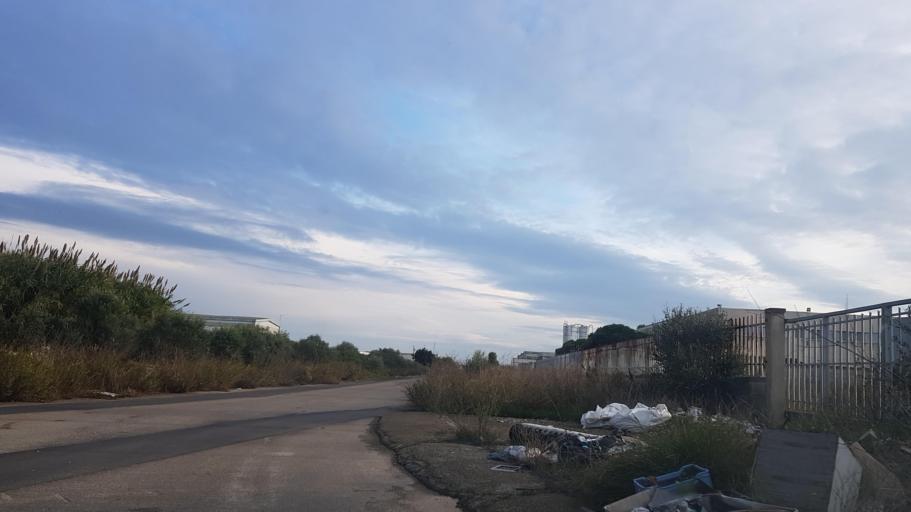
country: IT
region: Apulia
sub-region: Provincia di Brindisi
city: Materdomini
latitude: 40.6324
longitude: 17.9695
